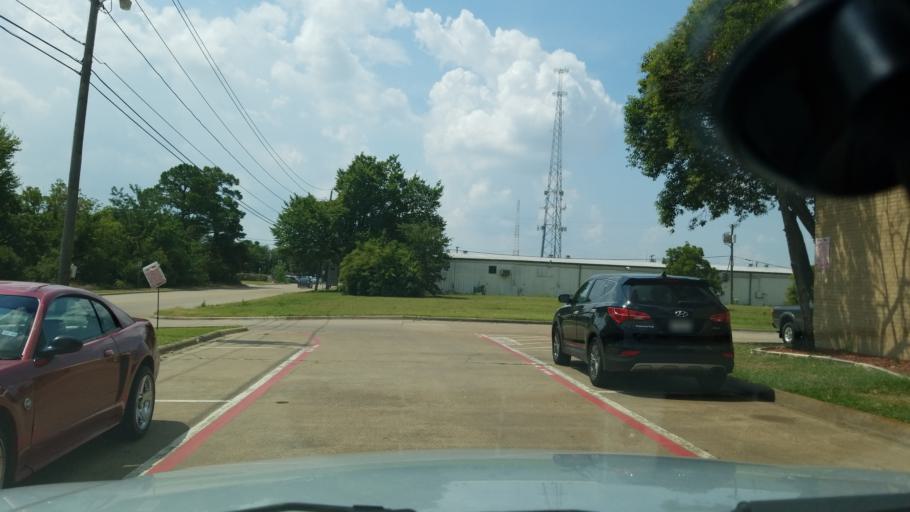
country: US
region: Texas
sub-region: Dallas County
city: Irving
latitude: 32.8347
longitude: -96.9118
